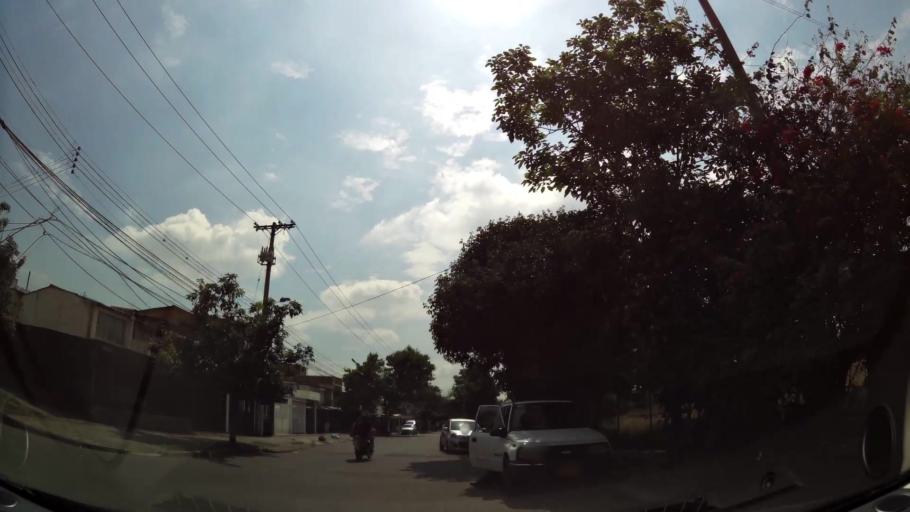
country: CO
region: Valle del Cauca
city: Cali
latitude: 3.4920
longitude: -76.5071
